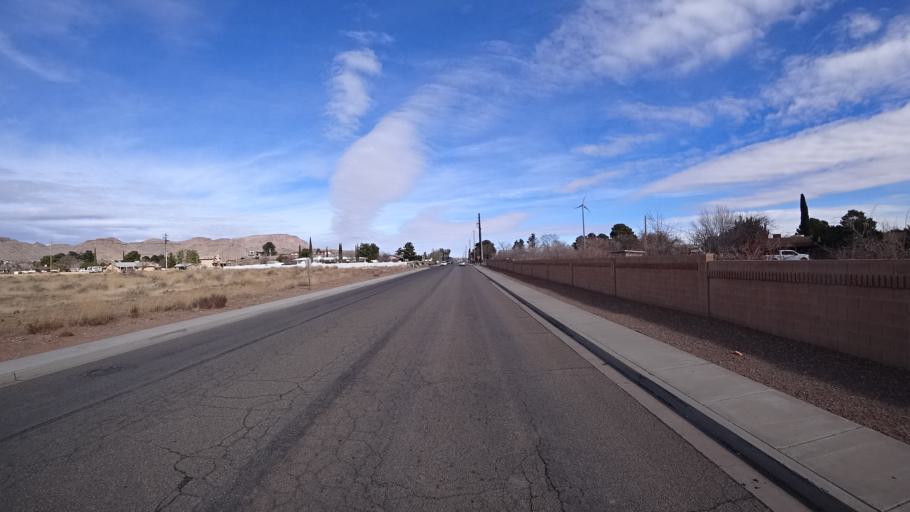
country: US
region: Arizona
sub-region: Mohave County
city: New Kingman-Butler
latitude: 35.2286
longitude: -114.0402
